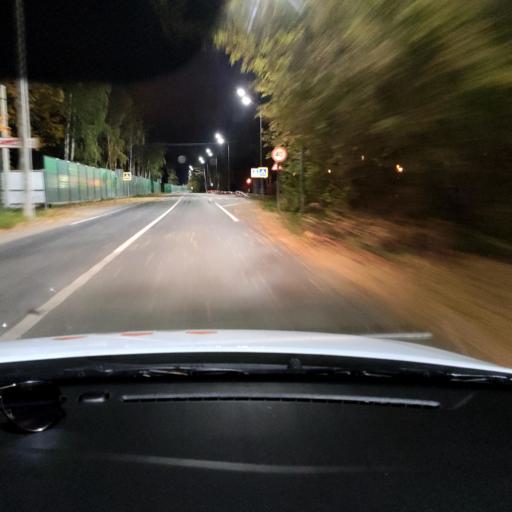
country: RU
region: Tatarstan
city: Verkhniy Uslon
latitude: 55.6245
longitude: 49.0138
